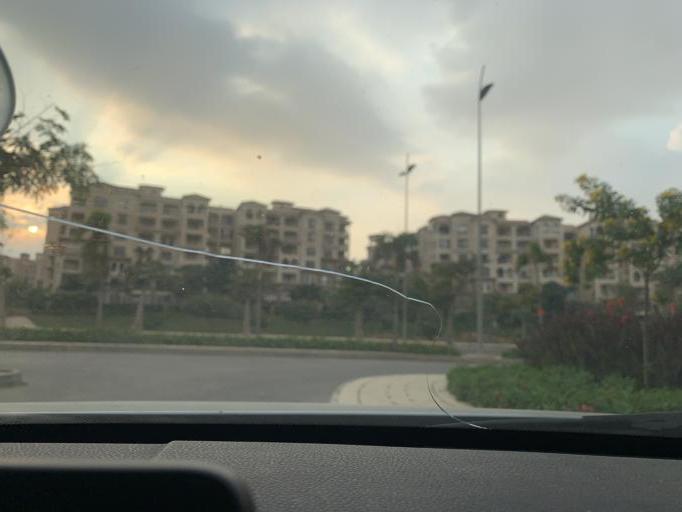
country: EG
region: Muhafazat al Qalyubiyah
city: Al Khankah
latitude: 30.1024
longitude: 31.6489
